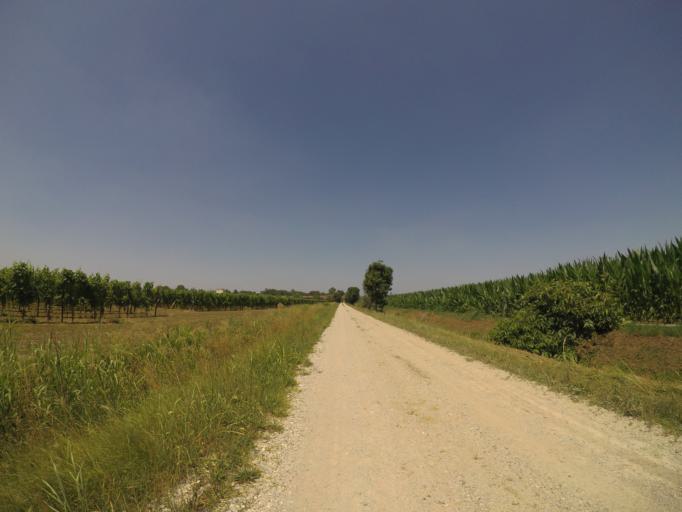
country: IT
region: Friuli Venezia Giulia
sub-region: Provincia di Udine
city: Bertiolo
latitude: 45.9440
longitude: 13.0159
